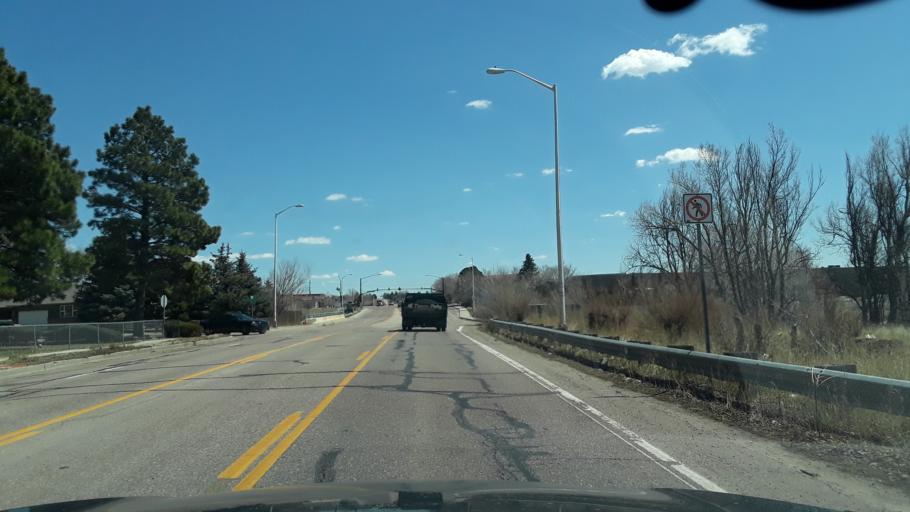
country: US
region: Colorado
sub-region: El Paso County
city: Cimarron Hills
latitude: 38.8465
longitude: -104.7260
